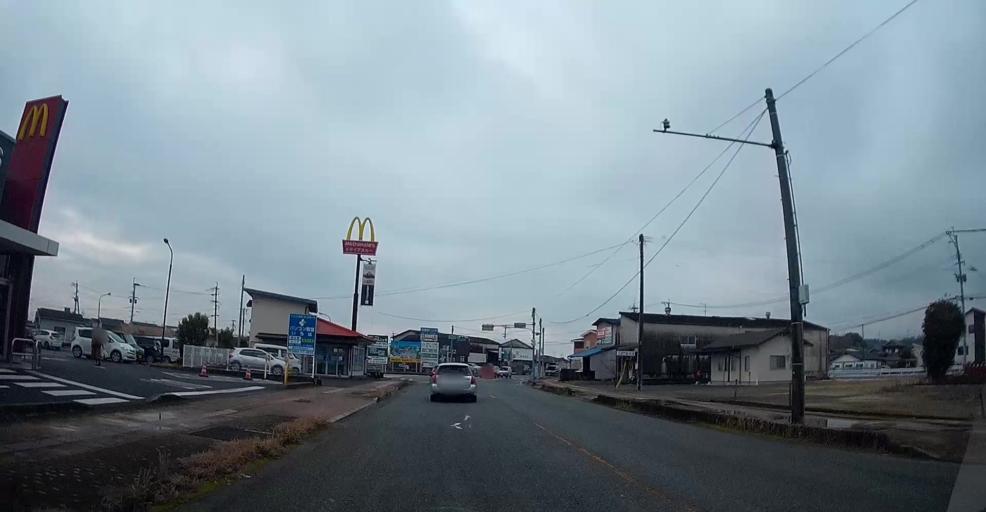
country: JP
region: Kumamoto
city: Matsubase
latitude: 32.6503
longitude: 130.6741
